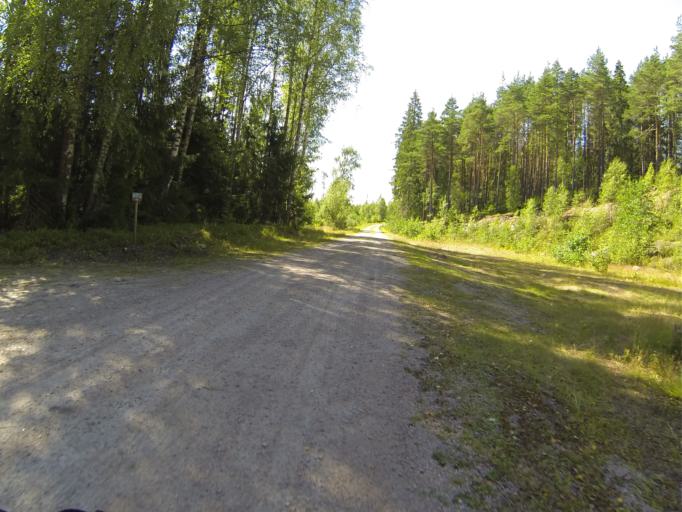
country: FI
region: Varsinais-Suomi
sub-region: Salo
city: Pernioe
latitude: 60.2863
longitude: 23.0755
